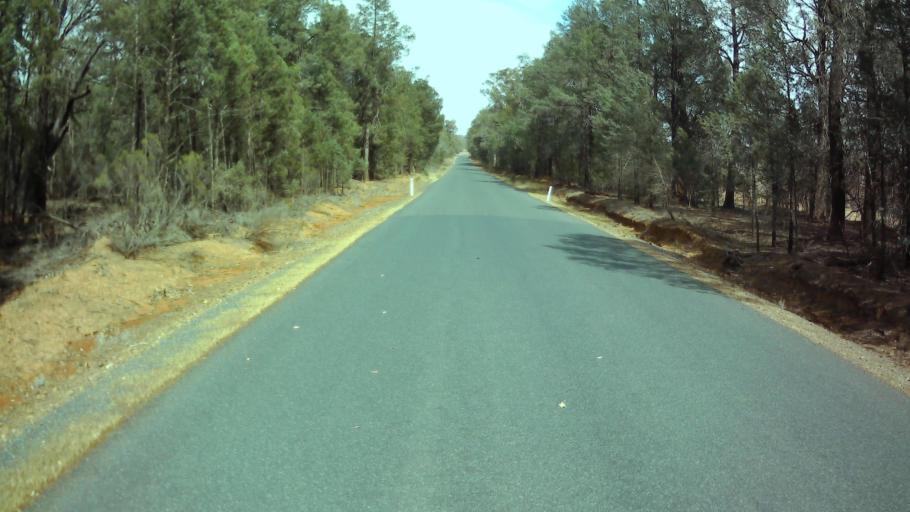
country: AU
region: New South Wales
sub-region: Weddin
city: Grenfell
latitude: -33.8022
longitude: 148.0158
